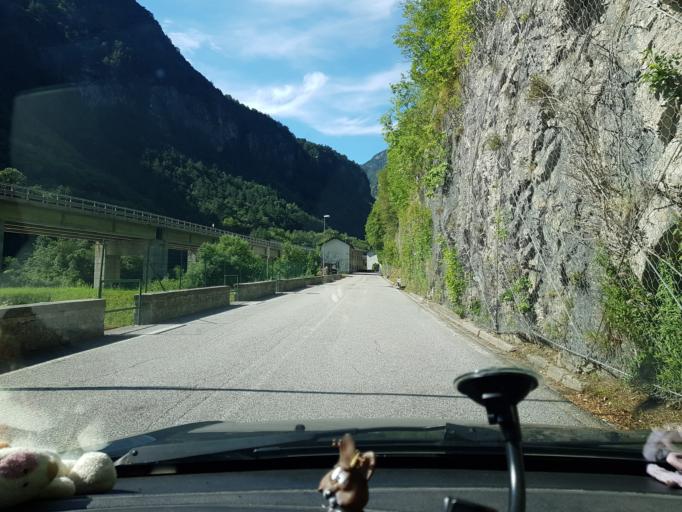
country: IT
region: Friuli Venezia Giulia
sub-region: Provincia di Udine
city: Dogna
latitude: 46.4463
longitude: 13.3145
